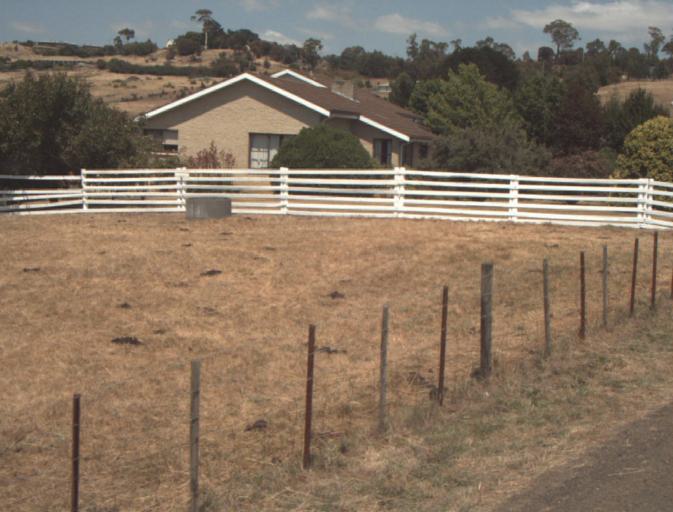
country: AU
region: Tasmania
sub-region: Launceston
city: Summerhill
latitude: -41.4930
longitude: 147.1764
